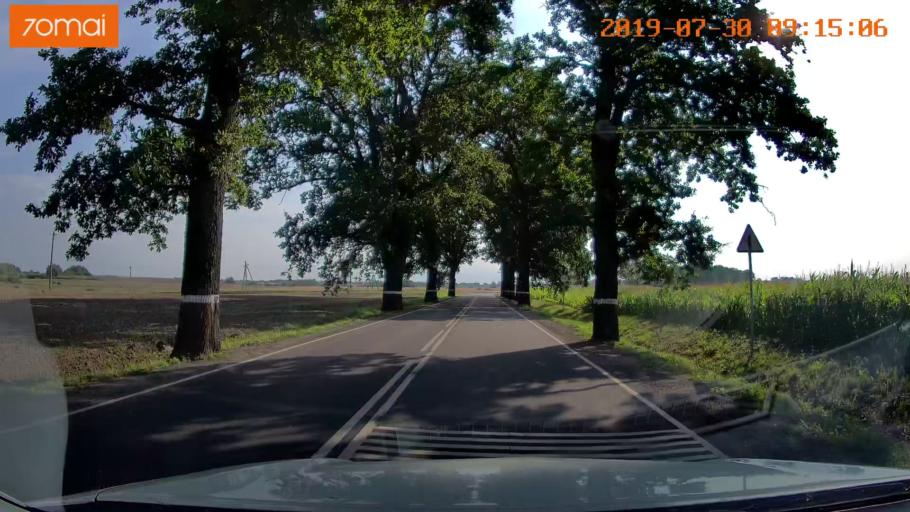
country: RU
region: Kaliningrad
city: Nesterov
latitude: 54.6334
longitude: 22.5330
